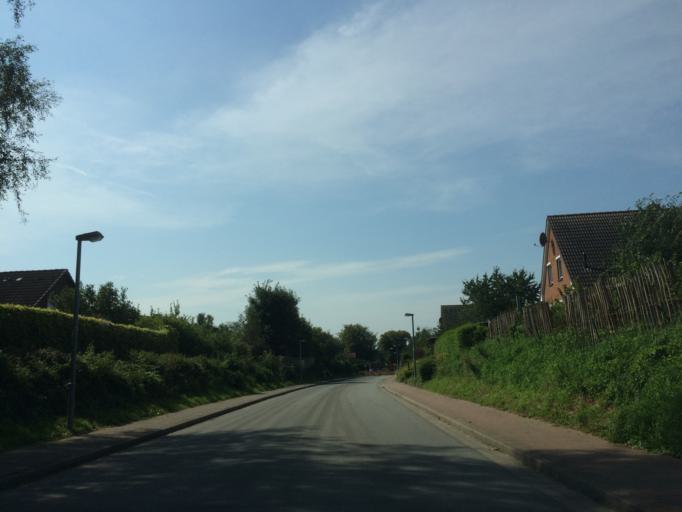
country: DE
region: Schleswig-Holstein
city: Holtsee
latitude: 54.4028
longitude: 9.8581
